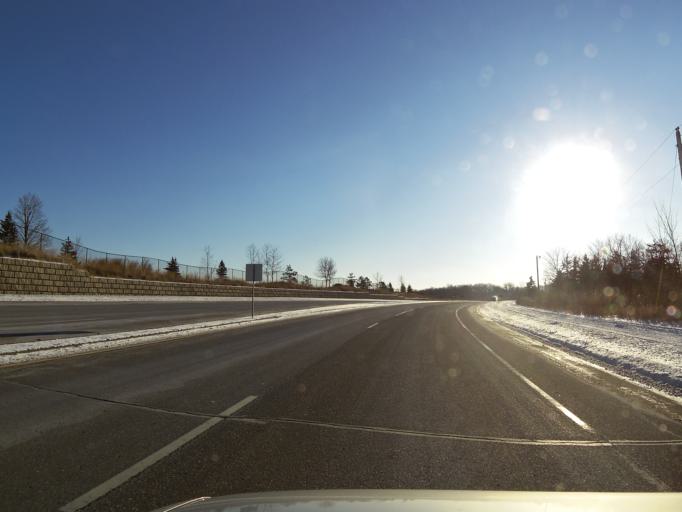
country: US
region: Minnesota
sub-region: Scott County
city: Prior Lake
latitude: 44.7264
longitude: -93.4850
